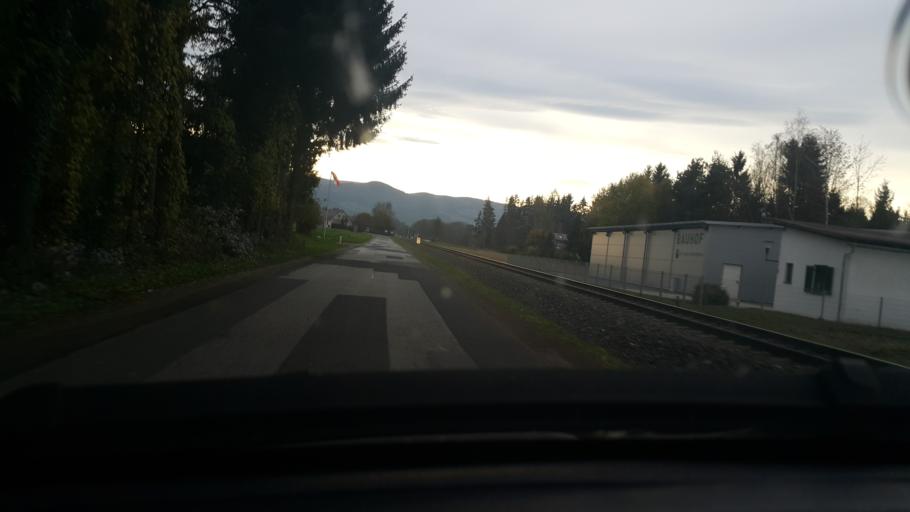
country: AT
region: Styria
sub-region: Politischer Bezirk Deutschlandsberg
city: Sankt Peter im Sulmtal
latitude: 46.7588
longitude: 15.2585
